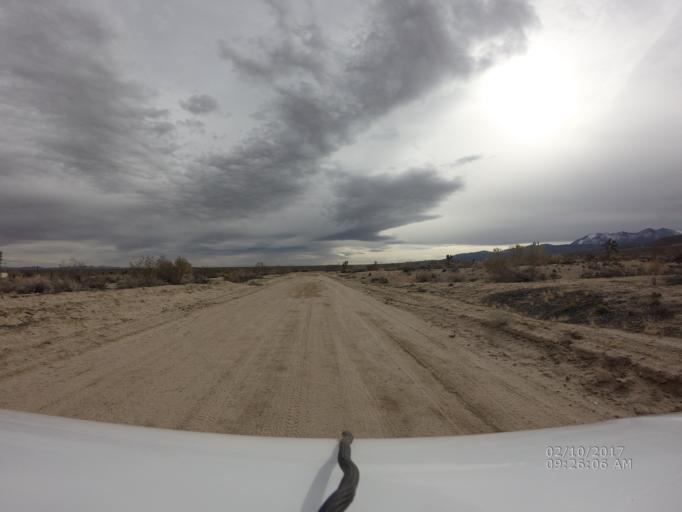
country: US
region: California
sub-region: Los Angeles County
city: Littlerock
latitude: 34.4972
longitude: -117.8893
